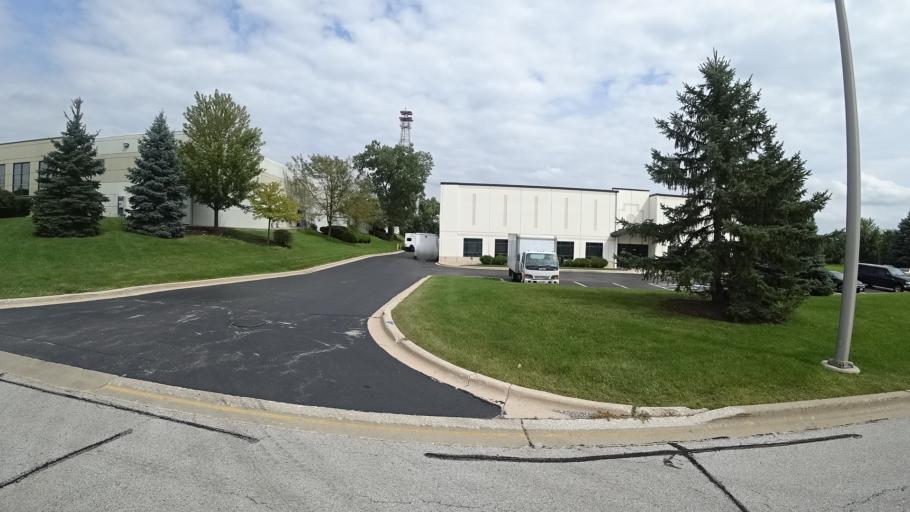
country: US
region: Illinois
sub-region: Cook County
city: Tinley Park
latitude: 41.5537
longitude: -87.8157
